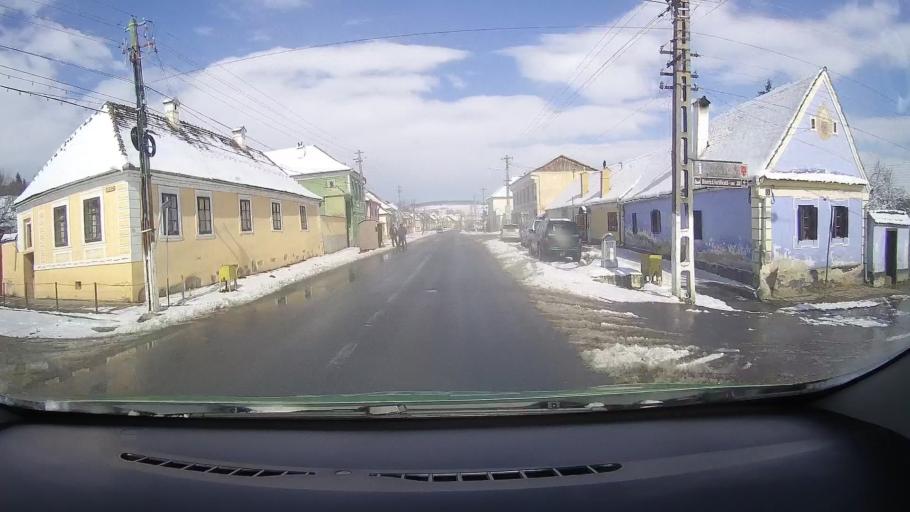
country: RO
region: Sibiu
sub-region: Comuna Altina
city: Altina
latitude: 45.9275
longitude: 24.4621
